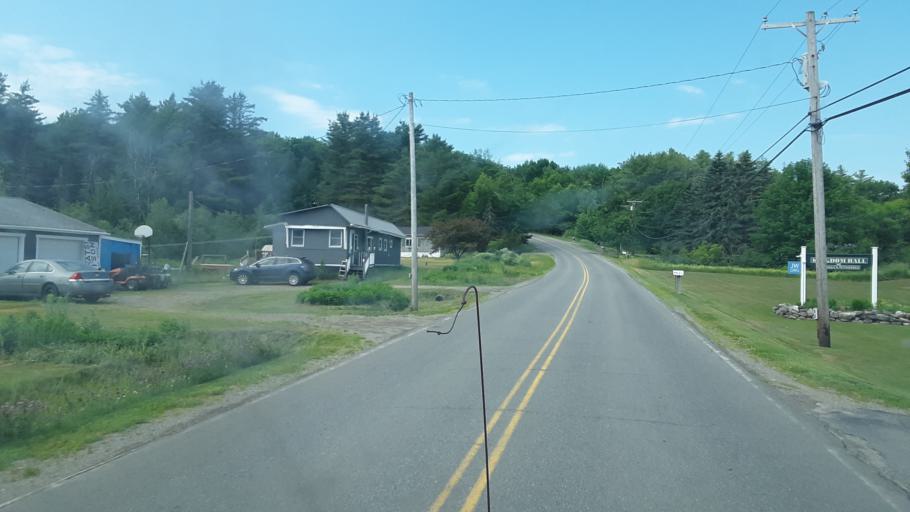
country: US
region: Maine
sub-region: Waldo County
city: Frankfort
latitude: 44.6125
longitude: -68.9305
